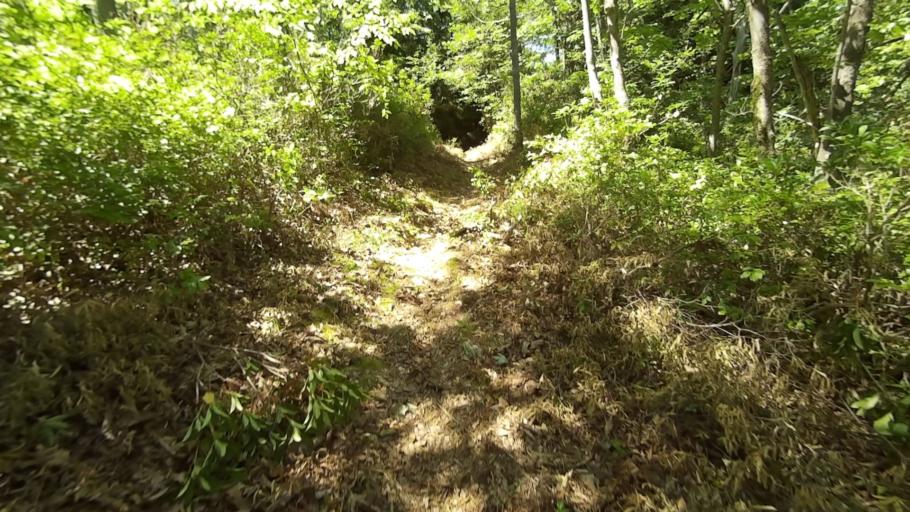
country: US
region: Pennsylvania
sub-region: Centre County
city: Boalsburg
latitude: 40.7202
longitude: -77.7828
